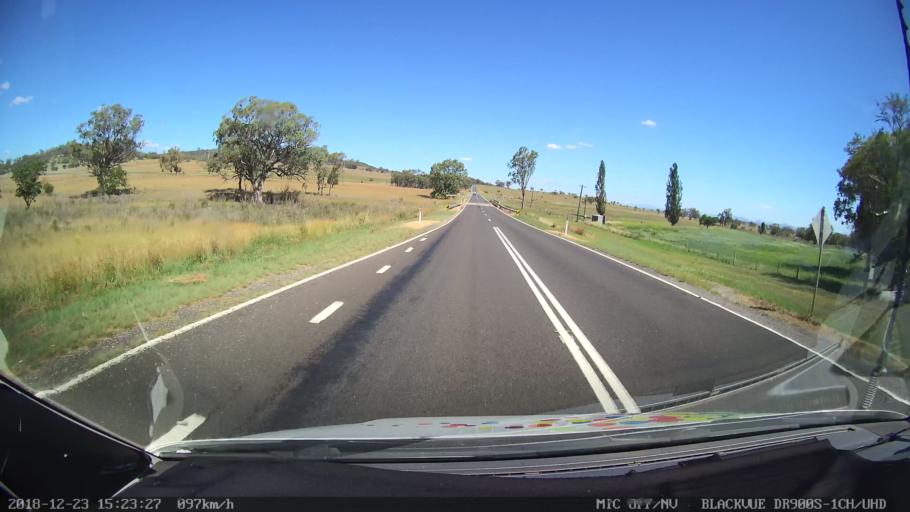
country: AU
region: New South Wales
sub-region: Tamworth Municipality
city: Manilla
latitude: -30.8803
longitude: 150.8141
